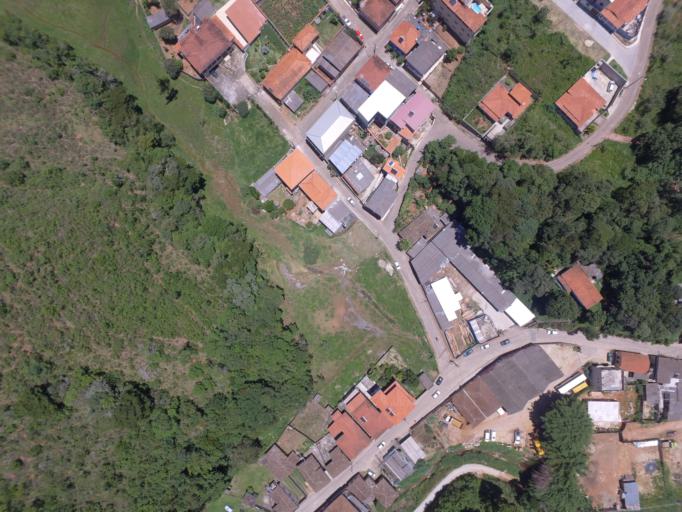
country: BR
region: Minas Gerais
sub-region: Tiradentes
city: Tiradentes
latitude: -21.0617
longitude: -44.0778
